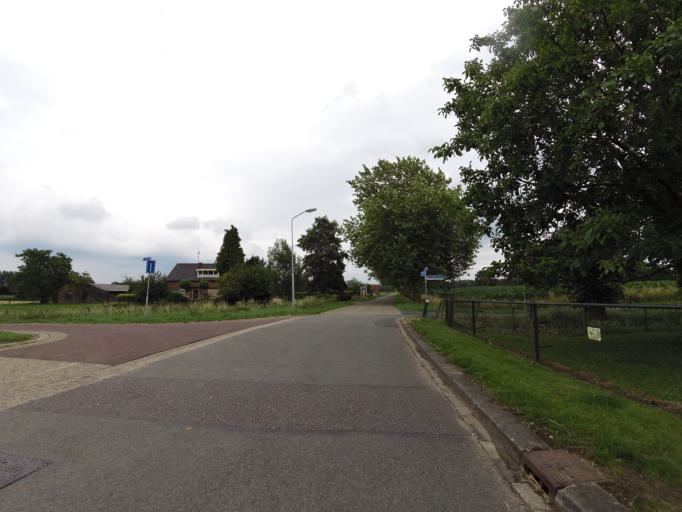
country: NL
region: Gelderland
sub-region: Gemeente Doesburg
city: Doesburg
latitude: 51.9958
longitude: 6.1468
